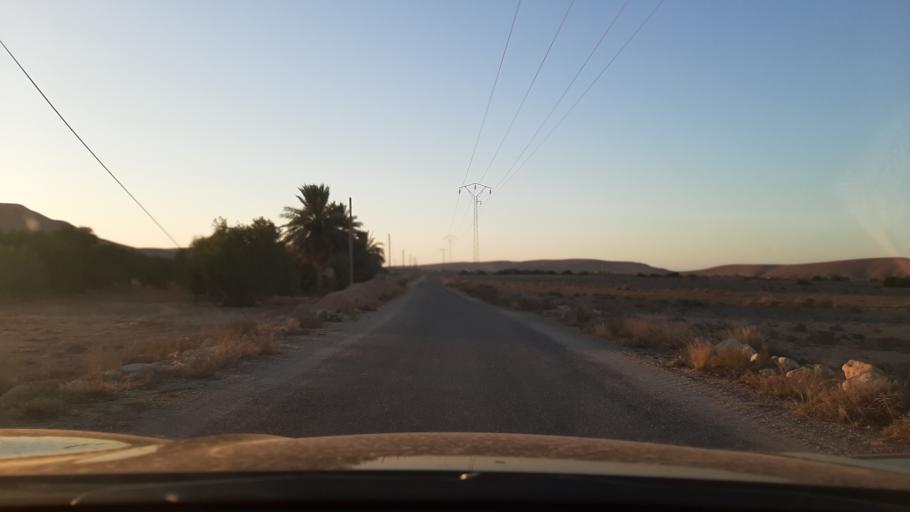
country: TN
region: Qabis
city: Matmata
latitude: 33.5451
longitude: 10.1923
